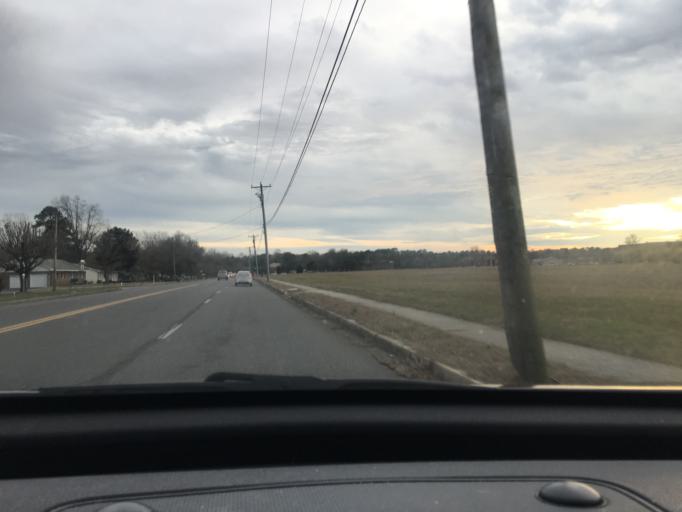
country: US
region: Maryland
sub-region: Wicomico County
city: Salisbury
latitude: 38.3641
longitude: -75.5678
